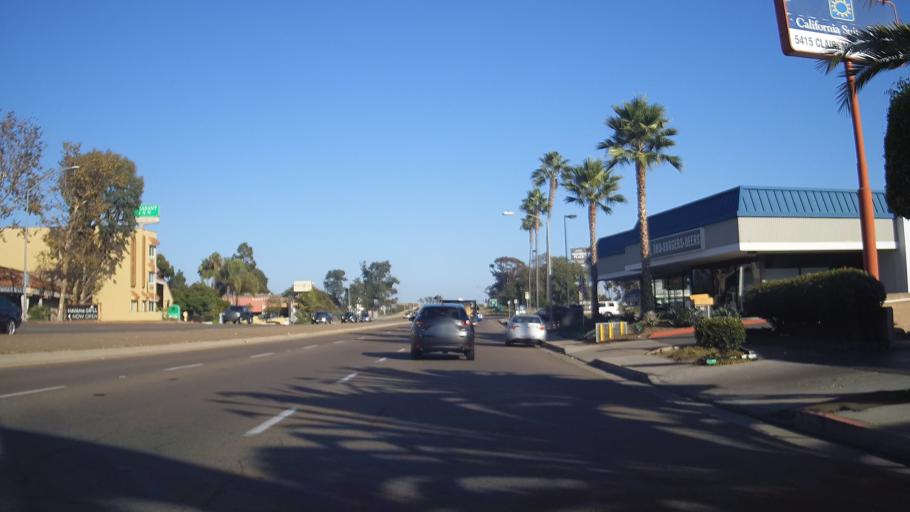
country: US
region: California
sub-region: San Diego County
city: La Jolla
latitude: 32.8342
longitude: -117.1744
